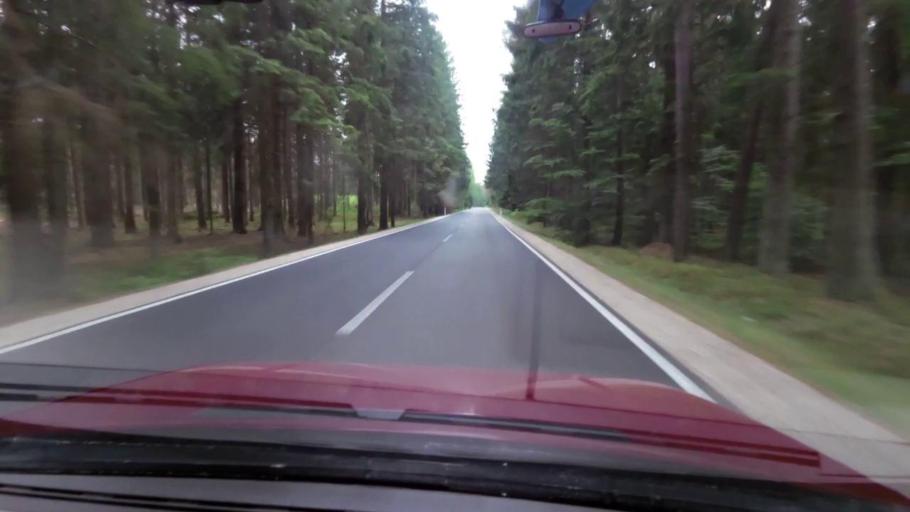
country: PL
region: West Pomeranian Voivodeship
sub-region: Powiat koszalinski
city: Polanow
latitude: 54.1440
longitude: 16.4832
